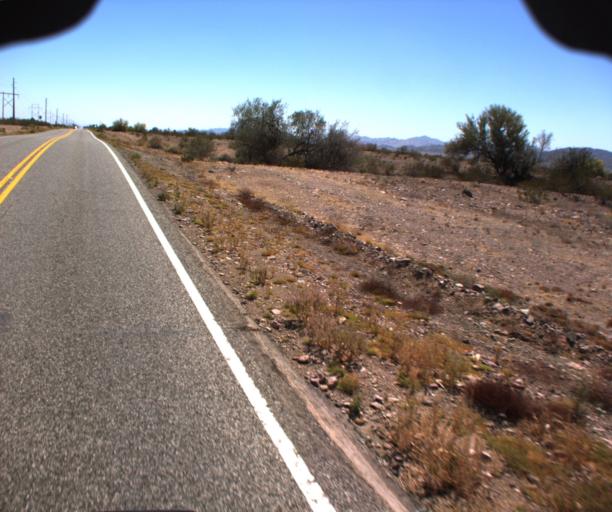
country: US
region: Arizona
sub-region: La Paz County
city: Quartzsite
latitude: 33.7554
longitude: -114.2170
